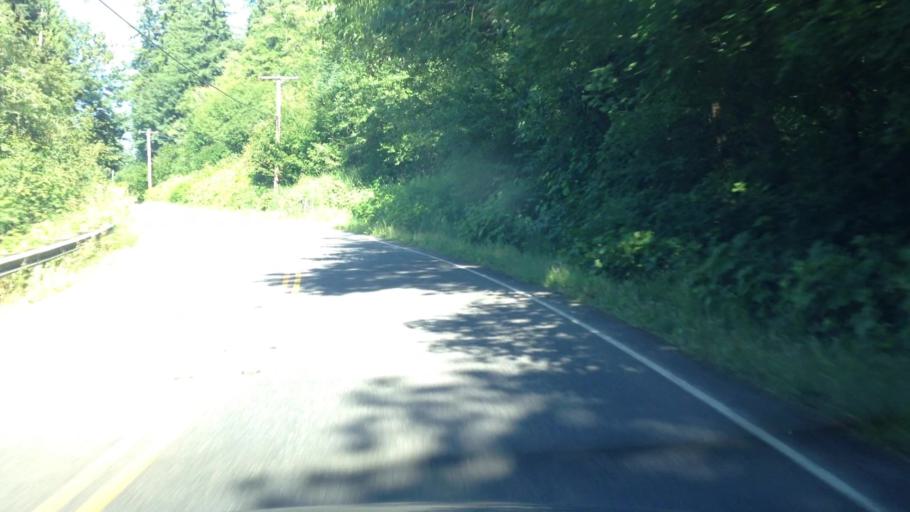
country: US
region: Washington
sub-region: King County
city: Duvall
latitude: 47.7445
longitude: -121.9349
